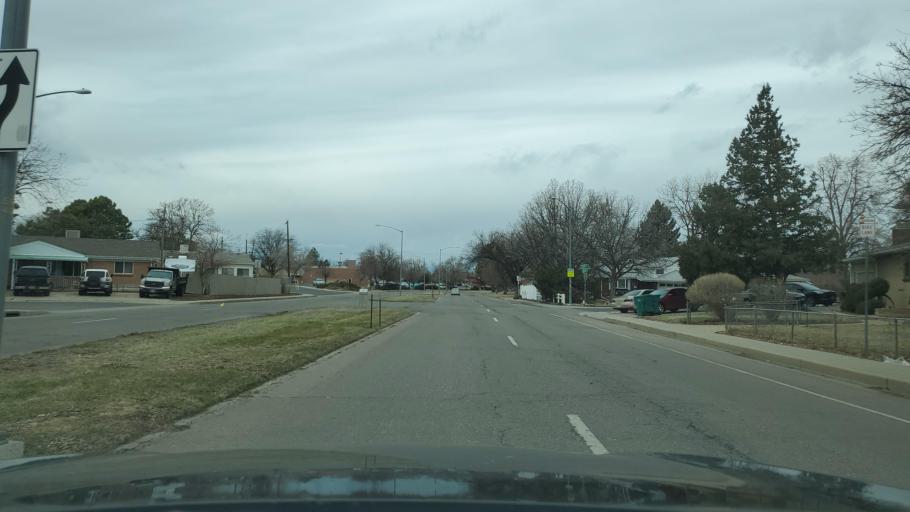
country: US
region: Colorado
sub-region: Adams County
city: Aurora
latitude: 39.7308
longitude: -104.8619
